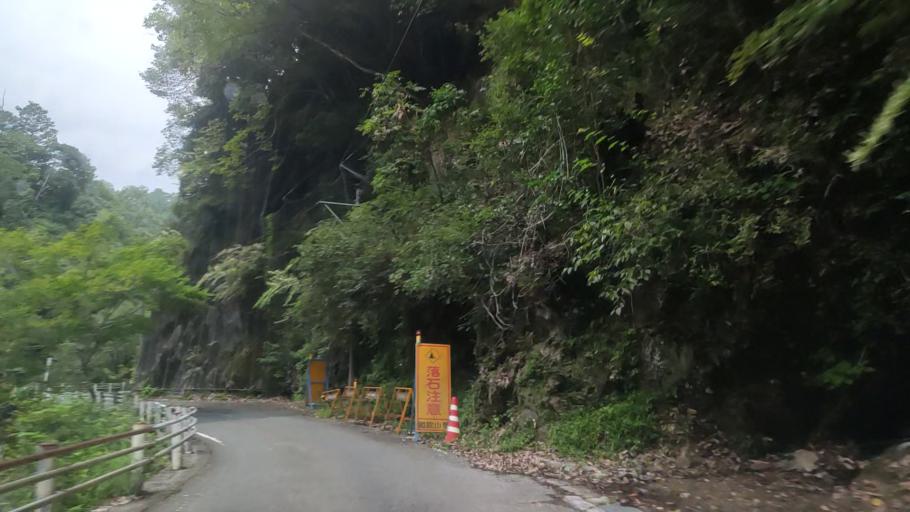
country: JP
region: Wakayama
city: Koya
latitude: 34.2647
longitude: 135.6453
